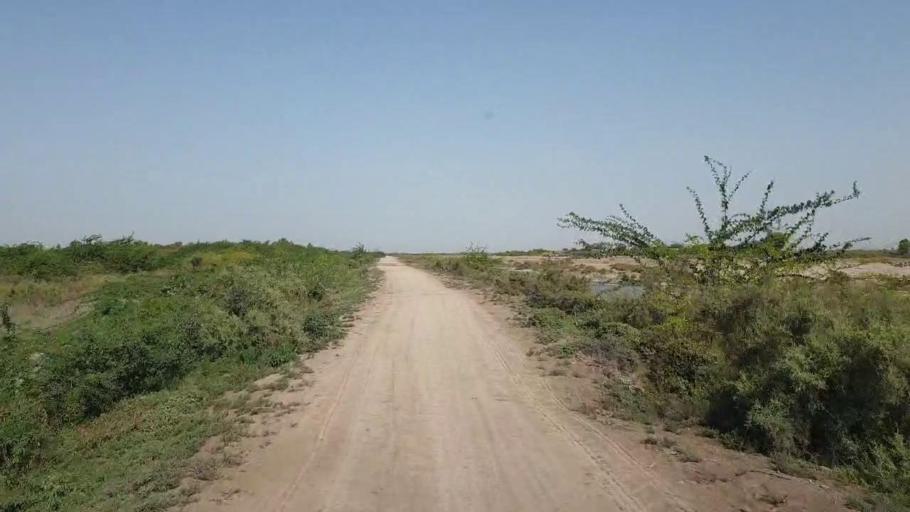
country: PK
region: Sindh
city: Tando Bago
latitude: 24.6469
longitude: 69.0717
